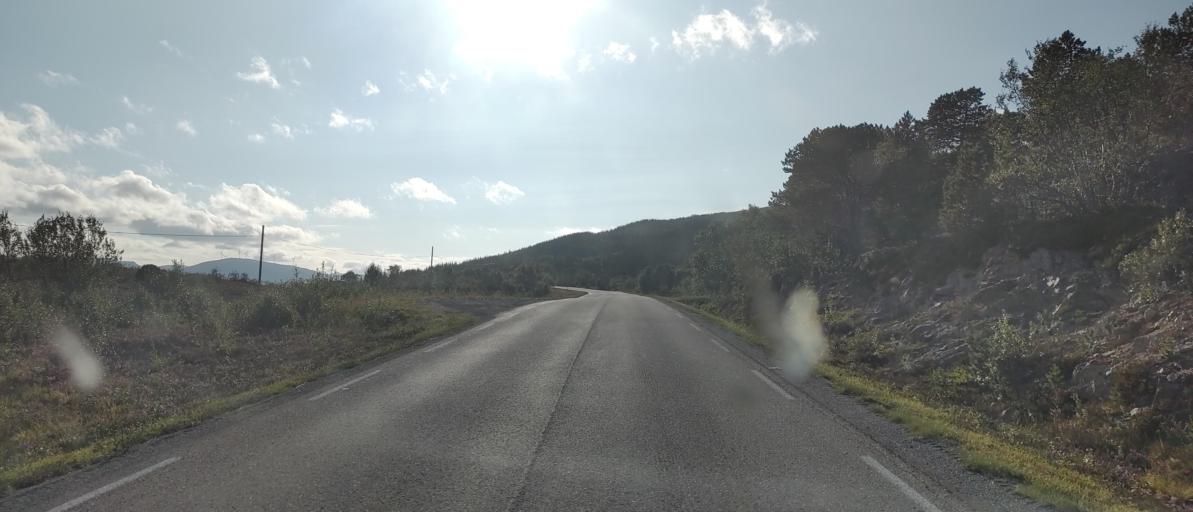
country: NO
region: Nordland
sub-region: Sortland
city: Sortland
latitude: 68.7956
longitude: 15.5199
